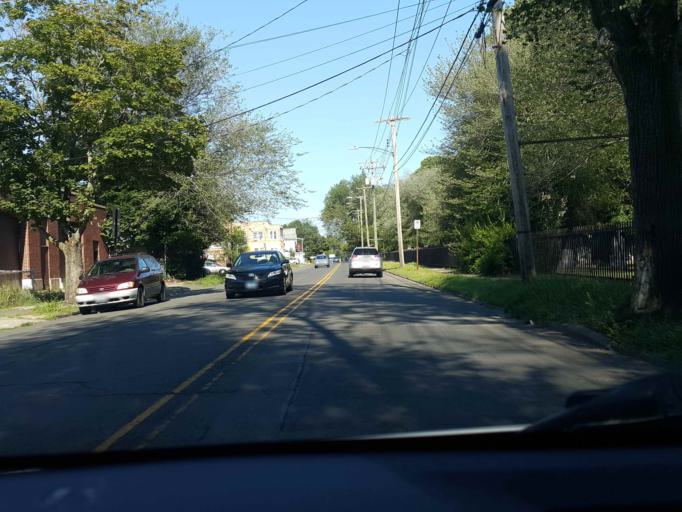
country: US
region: Connecticut
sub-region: New Haven County
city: New Haven
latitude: 41.2975
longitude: -72.9461
